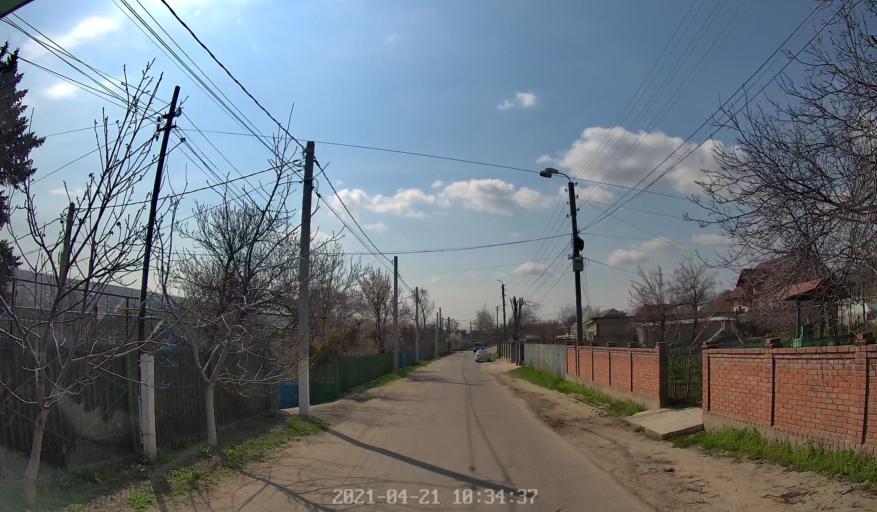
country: MD
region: Chisinau
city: Singera
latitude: 46.9818
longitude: 28.9372
